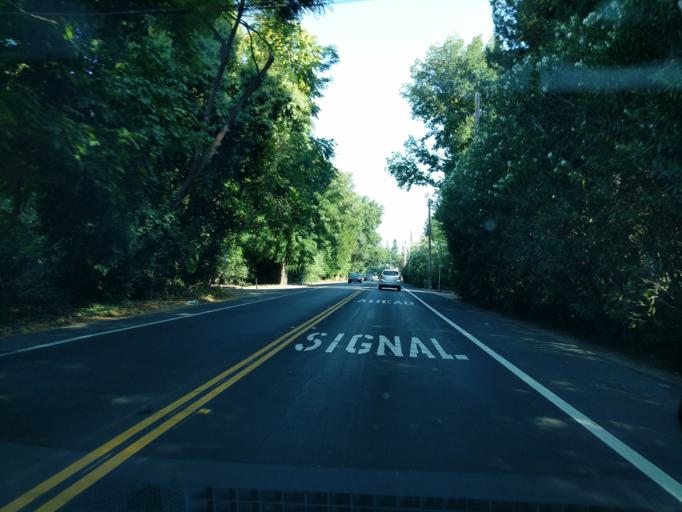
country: US
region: California
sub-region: Contra Costa County
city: Alamo
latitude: 37.8432
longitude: -122.0269
